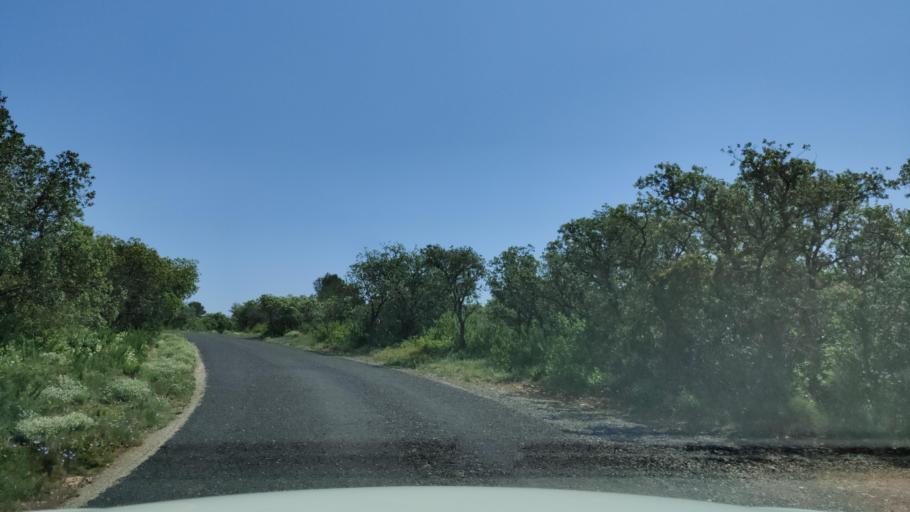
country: FR
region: Languedoc-Roussillon
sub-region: Departement des Pyrenees-Orientales
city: Estagel
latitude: 42.7892
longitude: 2.7347
